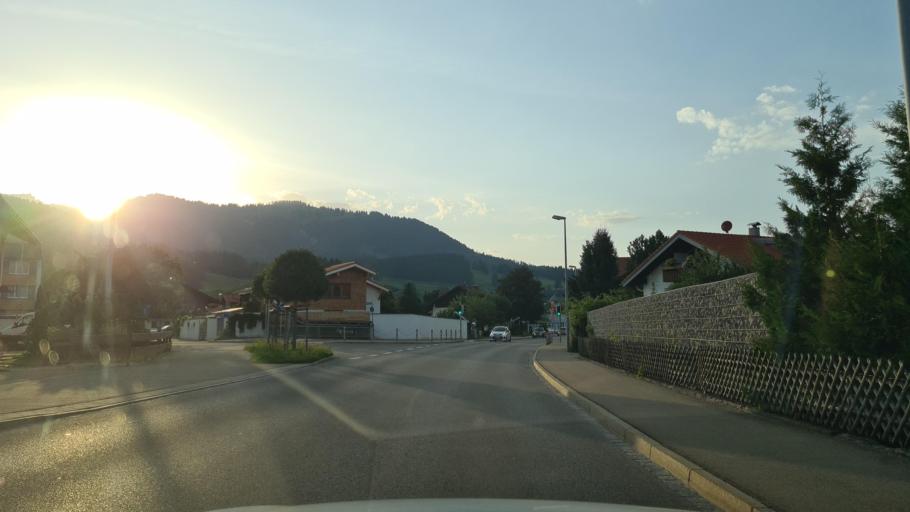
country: DE
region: Bavaria
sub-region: Swabia
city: Blaichach
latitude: 47.5209
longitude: 10.2654
